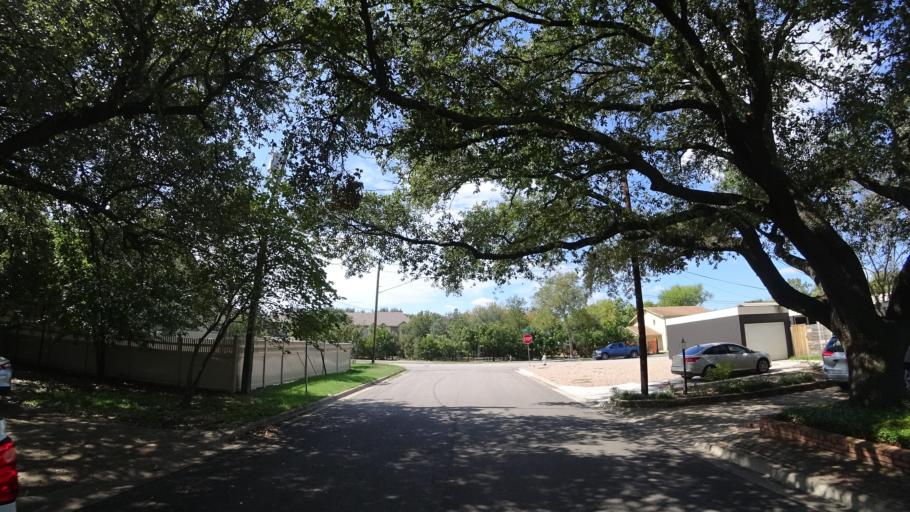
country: US
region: Texas
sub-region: Travis County
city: Austin
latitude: 30.3458
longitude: -97.7327
